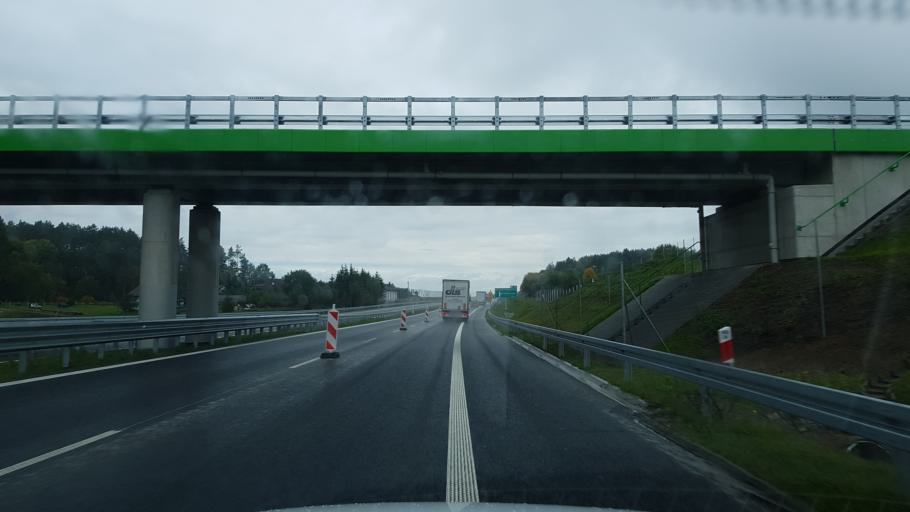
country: PL
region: West Pomeranian Voivodeship
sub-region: Powiat goleniowski
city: Przybiernow
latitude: 53.7372
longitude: 14.7740
